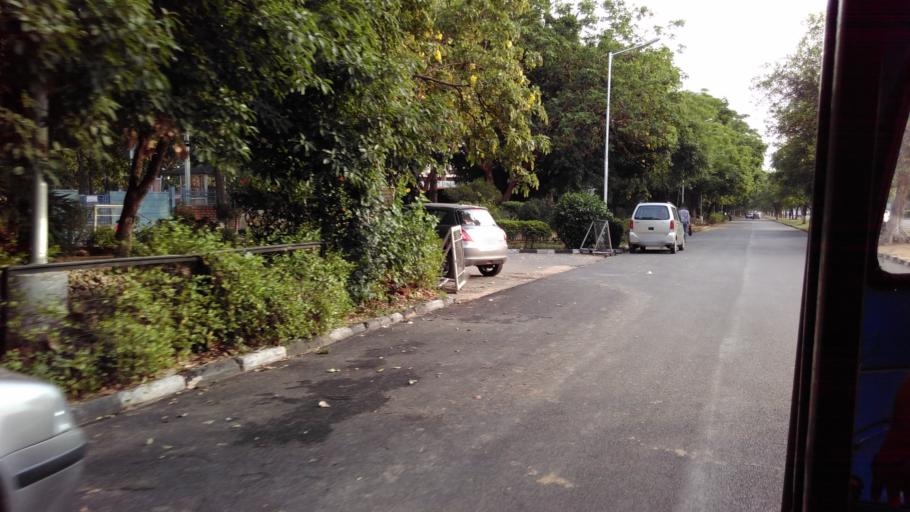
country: IN
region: Chandigarh
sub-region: Chandigarh
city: Chandigarh
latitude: 30.7457
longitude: 76.7846
